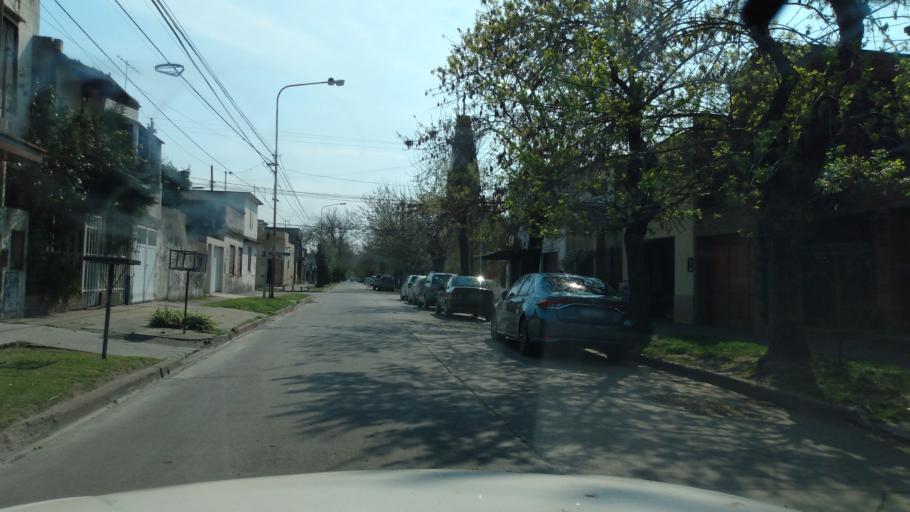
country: AR
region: Buenos Aires
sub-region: Partido de Lujan
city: Lujan
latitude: -34.5737
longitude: -59.1080
